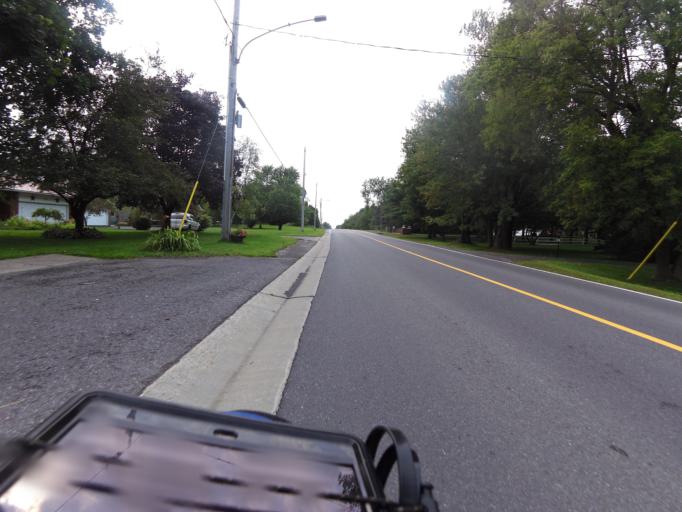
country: CA
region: Ontario
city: Casselman
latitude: 45.1761
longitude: -75.2889
